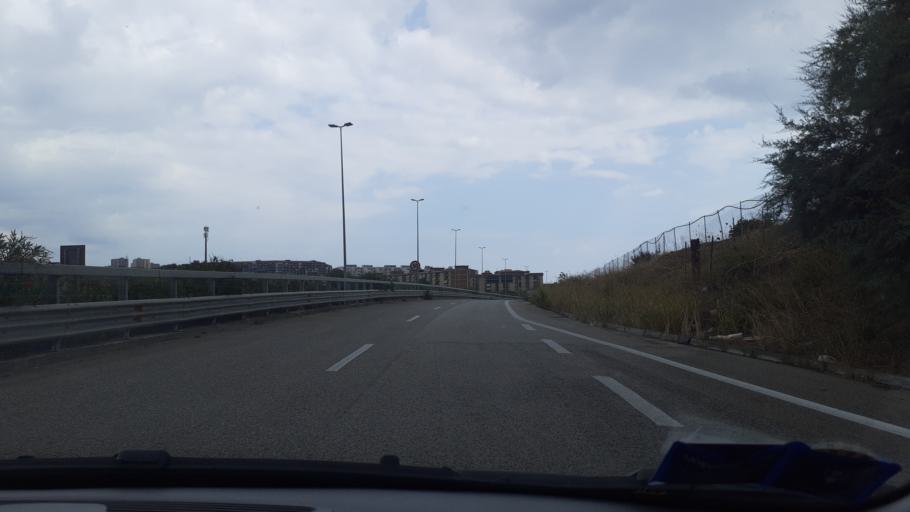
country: IT
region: Sicily
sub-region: Catania
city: Catania
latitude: 37.4763
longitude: 15.0431
